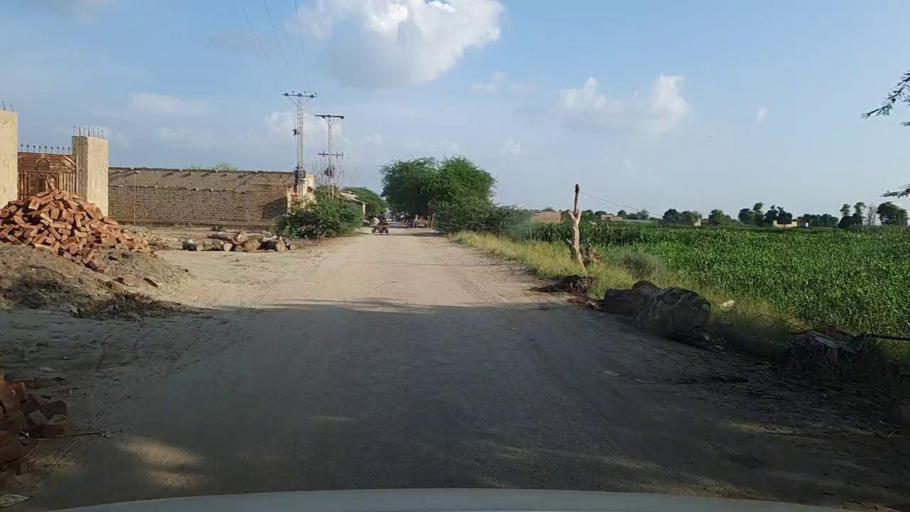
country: PK
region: Sindh
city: Hingorja
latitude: 27.0911
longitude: 68.4171
